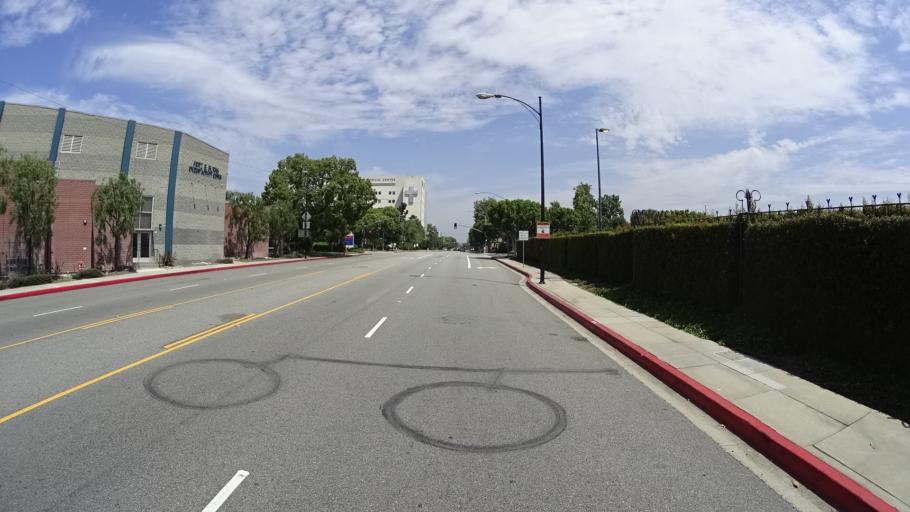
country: US
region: California
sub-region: Los Angeles County
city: Universal City
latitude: 34.1550
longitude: -118.3267
